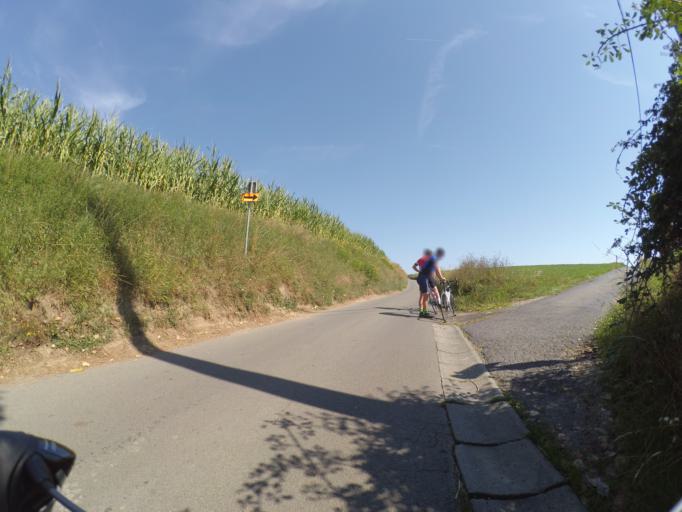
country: BE
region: Flanders
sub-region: Provincie Oost-Vlaanderen
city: Oudenaarde
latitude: 50.8231
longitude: 3.6272
